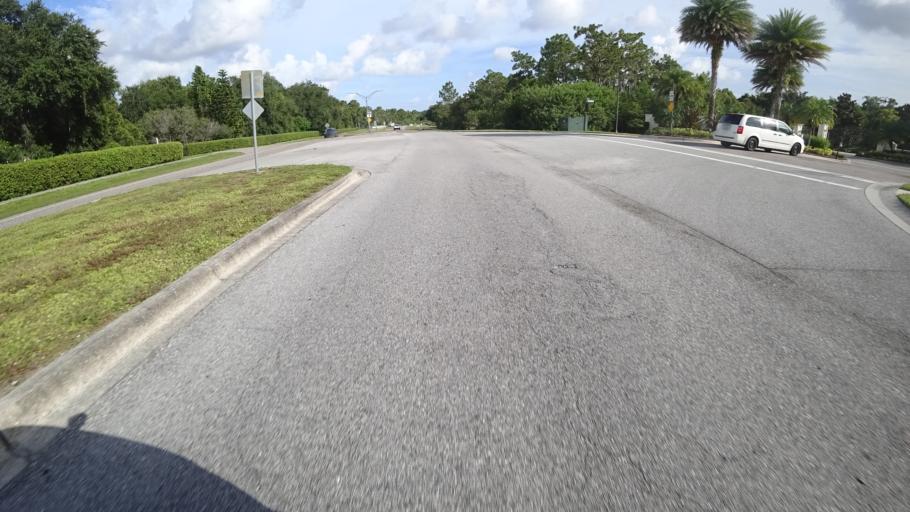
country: US
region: Florida
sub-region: Sarasota County
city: Desoto Lakes
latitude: 27.4104
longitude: -82.4633
